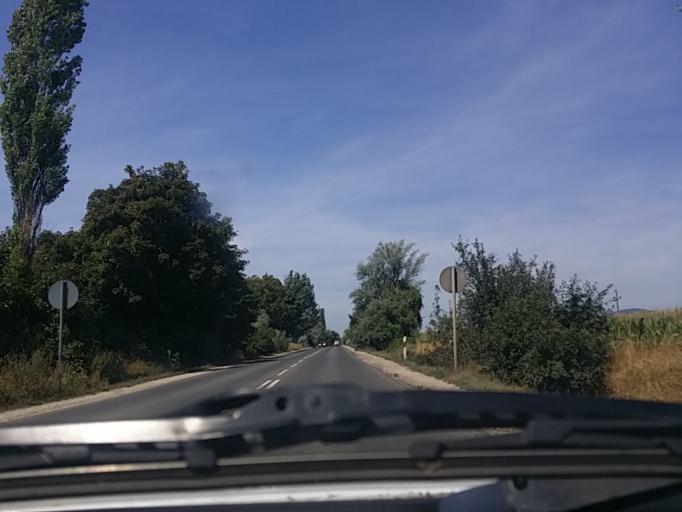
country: HU
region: Pest
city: Solymar
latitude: 47.6024
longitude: 18.9553
